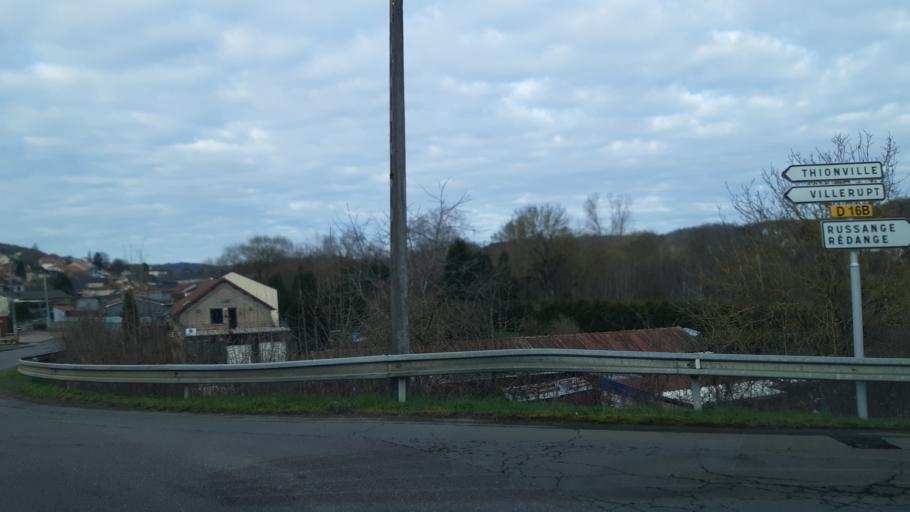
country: FR
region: Lorraine
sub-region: Departement de la Moselle
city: Audun-le-Tiche
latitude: 49.4776
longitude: 5.9555
